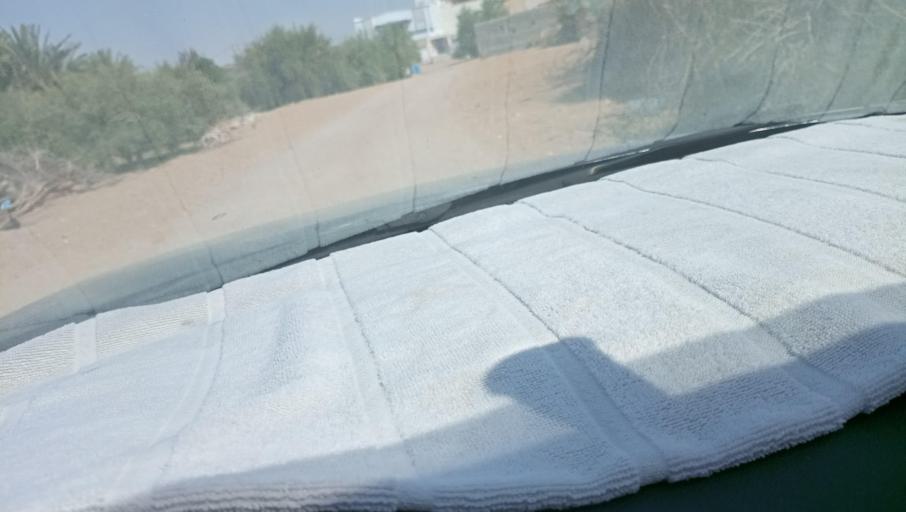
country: TN
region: Tataouine
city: Tataouine
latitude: 32.9808
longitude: 10.3826
